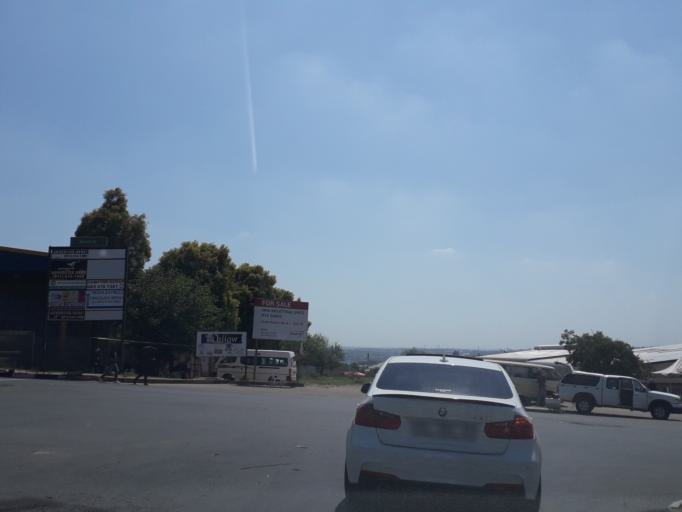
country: ZA
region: Gauteng
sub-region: West Rand District Municipality
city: Muldersdriseloop
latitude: -26.0273
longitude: 27.9498
